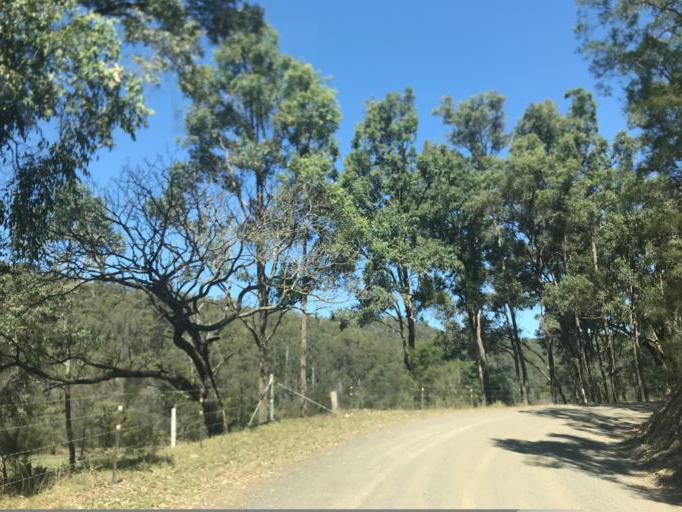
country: AU
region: New South Wales
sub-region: Wyong Shire
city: Little Jilliby
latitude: -33.1988
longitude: 150.9990
